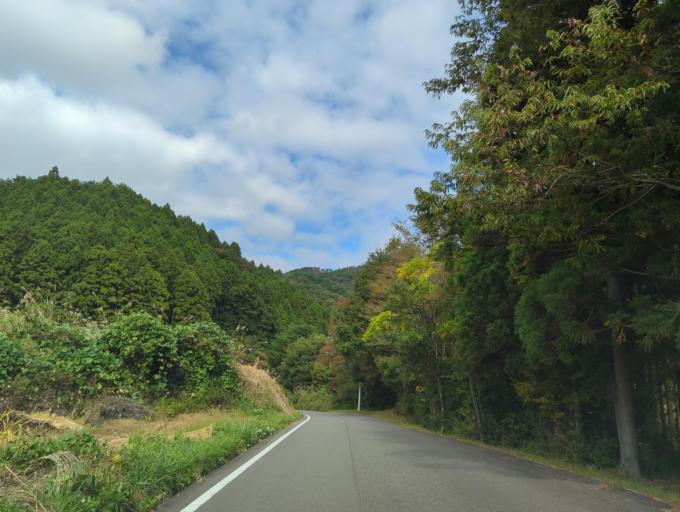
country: JP
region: Fukushima
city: Motomiya
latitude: 37.5108
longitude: 140.3271
